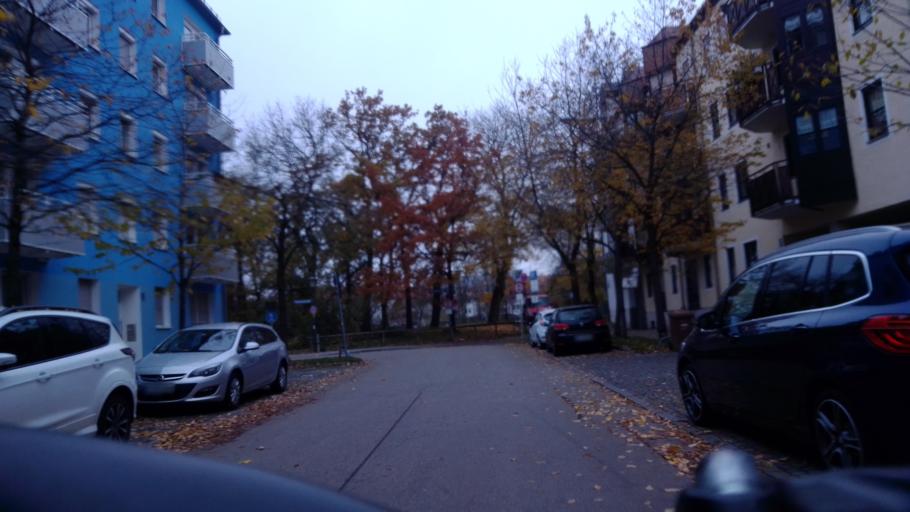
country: DE
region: Bavaria
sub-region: Upper Bavaria
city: Munich
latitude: 48.1207
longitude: 11.5387
